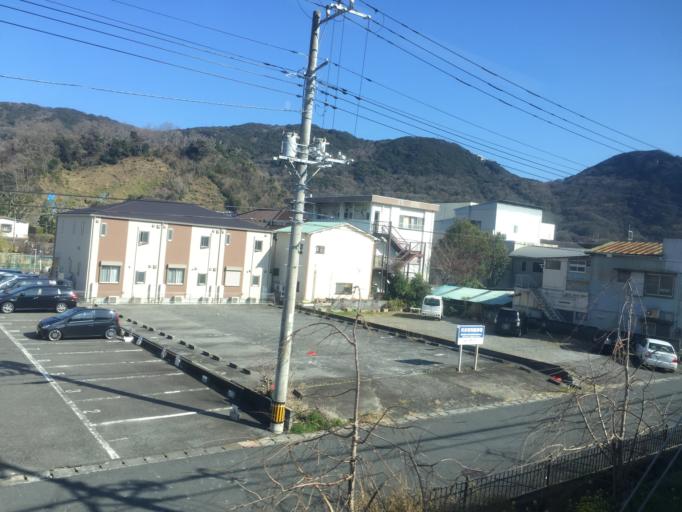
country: JP
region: Shizuoka
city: Shimoda
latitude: 34.6851
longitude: 138.9448
